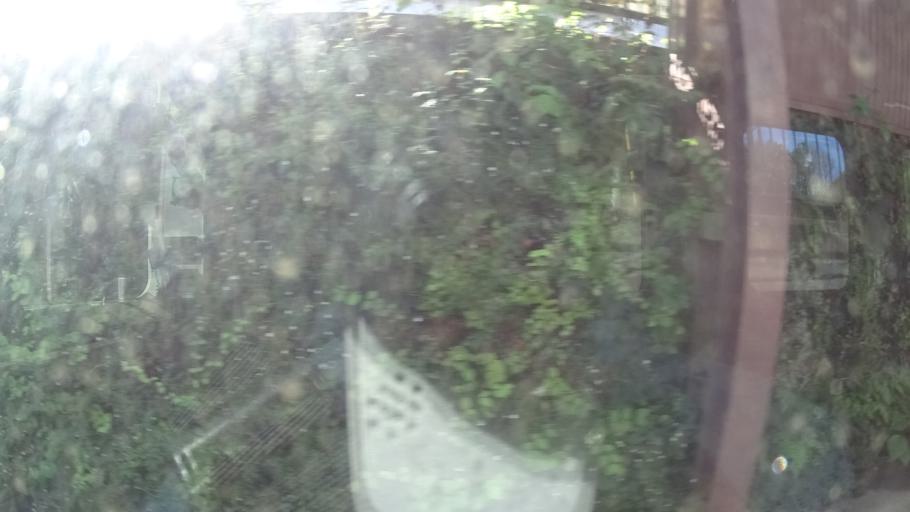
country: JP
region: Kanagawa
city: Kamakura
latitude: 35.3097
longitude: 139.5294
